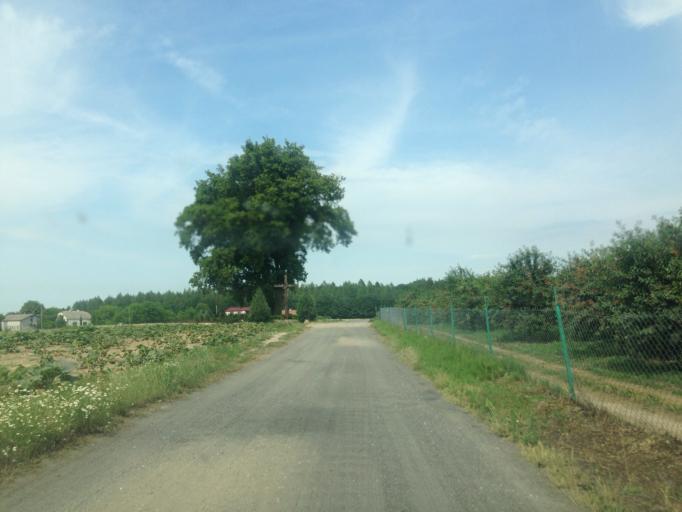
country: PL
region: Kujawsko-Pomorskie
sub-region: Powiat brodnicki
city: Bobrowo
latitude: 53.2637
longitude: 19.3008
